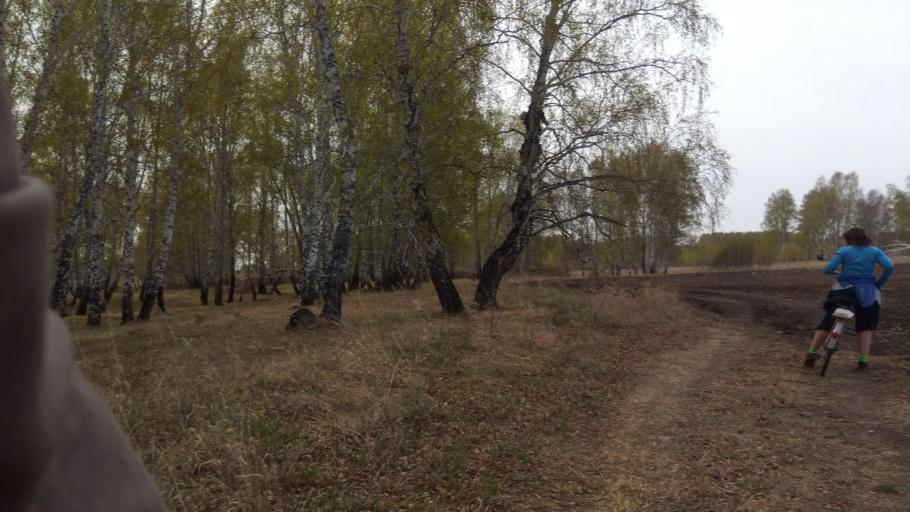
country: RU
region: Chelyabinsk
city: Timiryazevskiy
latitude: 55.0095
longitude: 60.8598
